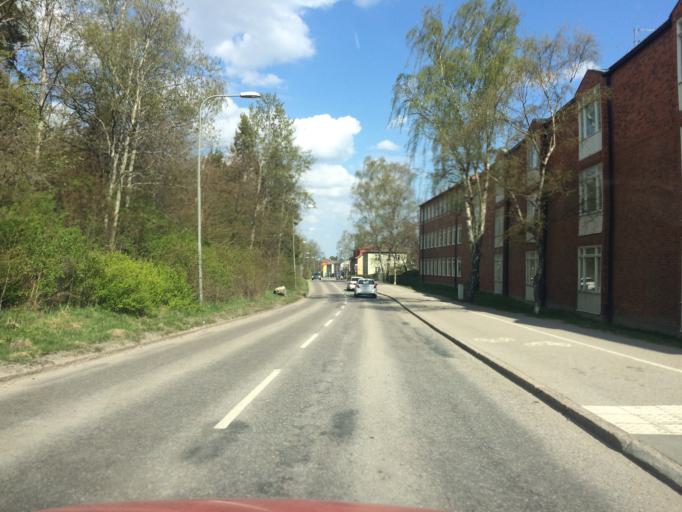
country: SE
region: Stockholm
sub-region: Huddinge Kommun
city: Segeltorp
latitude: 59.2972
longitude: 17.9563
